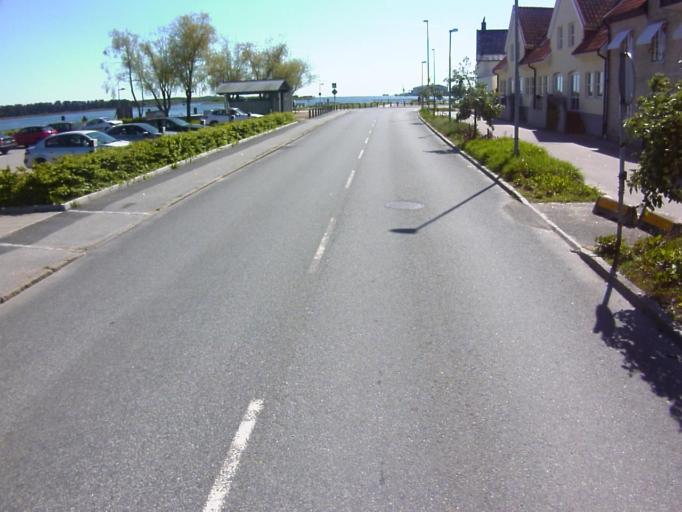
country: SE
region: Blekinge
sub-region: Solvesborgs Kommun
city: Soelvesborg
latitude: 56.0516
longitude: 14.5893
